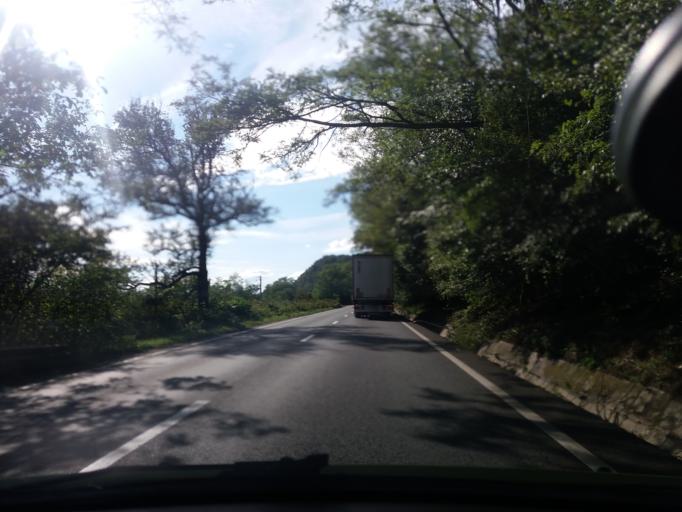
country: RO
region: Arad
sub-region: Comuna Varadia de Mures
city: Varadia de Mures
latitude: 46.0049
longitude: 22.1891
